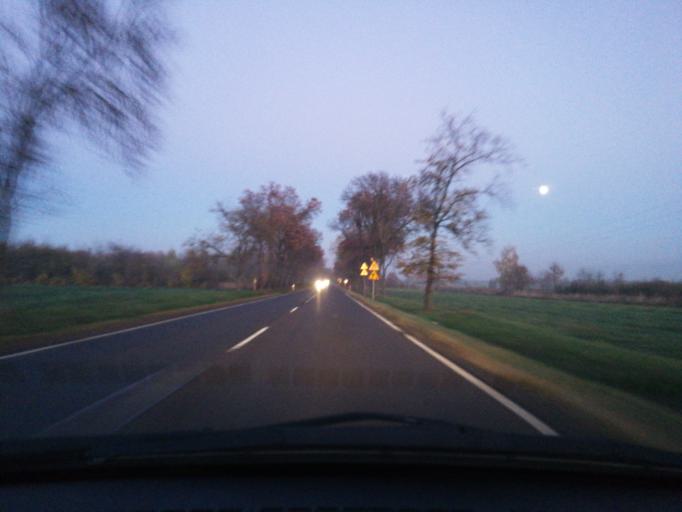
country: PL
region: Lodz Voivodeship
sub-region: Powiat brzezinski
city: Rogow
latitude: 51.8063
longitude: 19.8843
